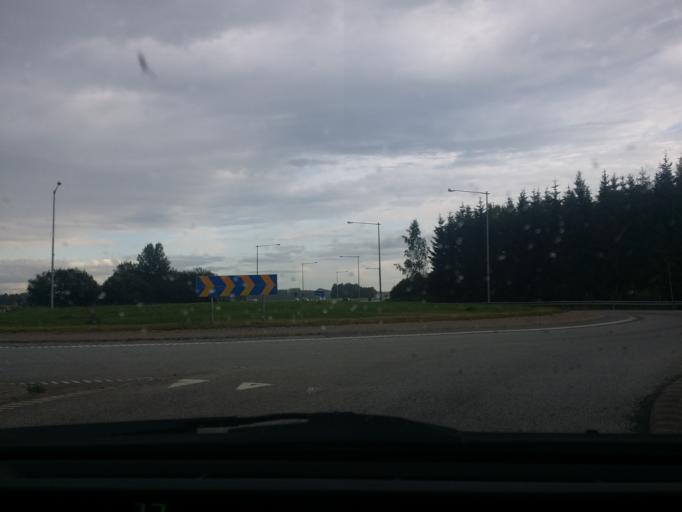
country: SE
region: OErebro
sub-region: Orebro Kommun
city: Hovsta
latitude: 59.4236
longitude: 15.1772
